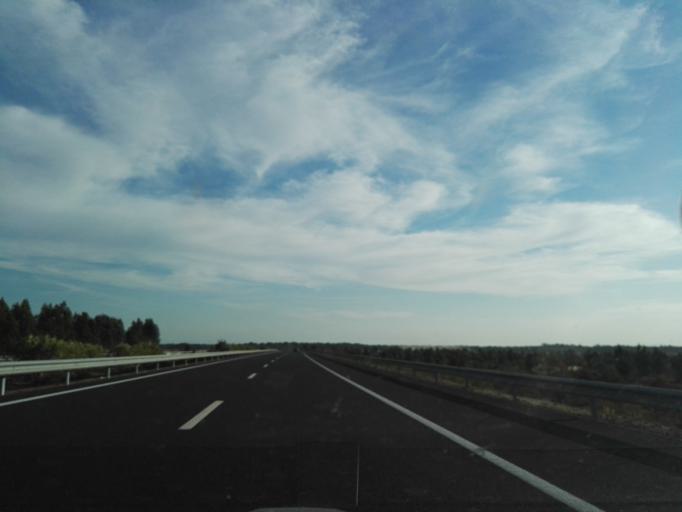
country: PT
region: Santarem
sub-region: Benavente
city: Poceirao
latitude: 38.7635
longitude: -8.6834
